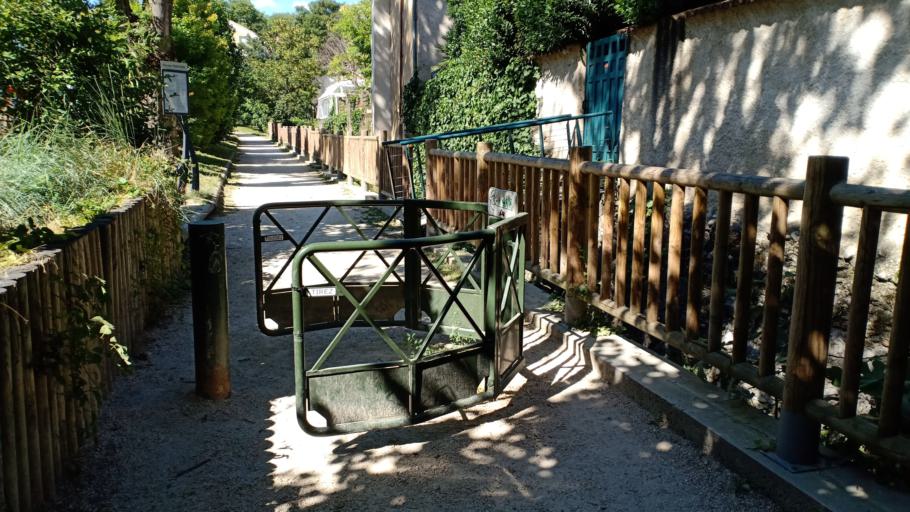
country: FR
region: Rhone-Alpes
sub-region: Departement de l'Ardeche
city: Guilherand-Granges
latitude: 44.9264
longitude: 4.8850
